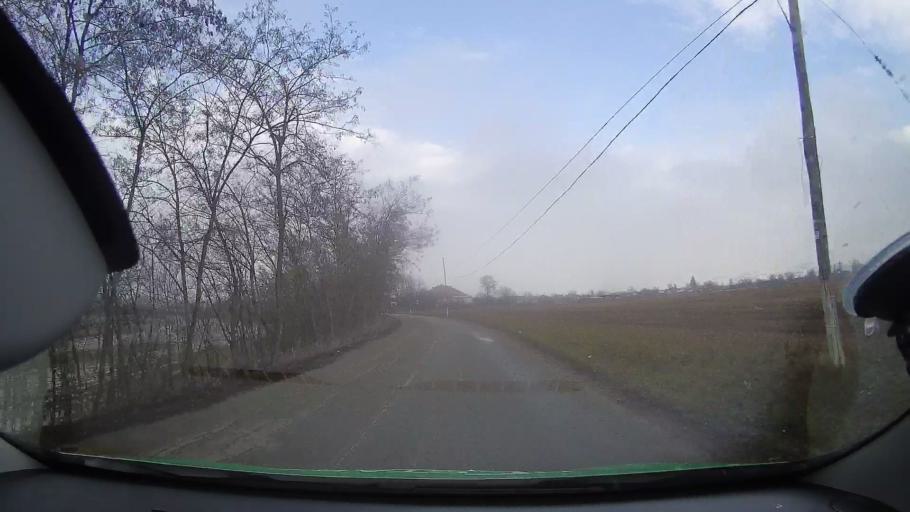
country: RO
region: Alba
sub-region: Comuna Noslac
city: Noslac
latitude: 46.4212
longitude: 23.9891
